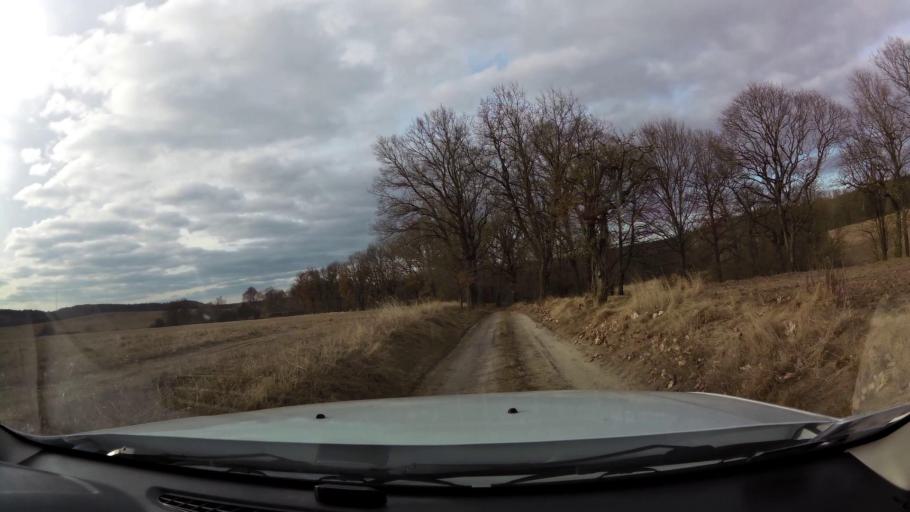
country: PL
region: West Pomeranian Voivodeship
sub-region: Powiat drawski
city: Drawsko Pomorskie
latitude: 53.5181
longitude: 15.7113
